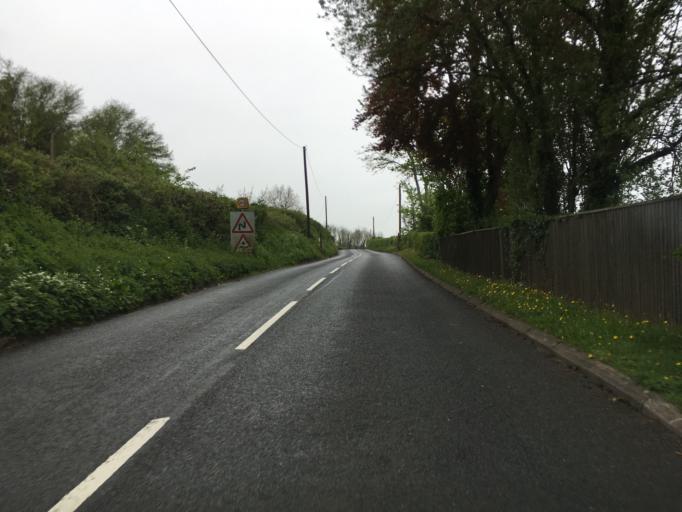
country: GB
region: England
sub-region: Bath and North East Somerset
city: Compton Martin
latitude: 51.3160
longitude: -2.6740
